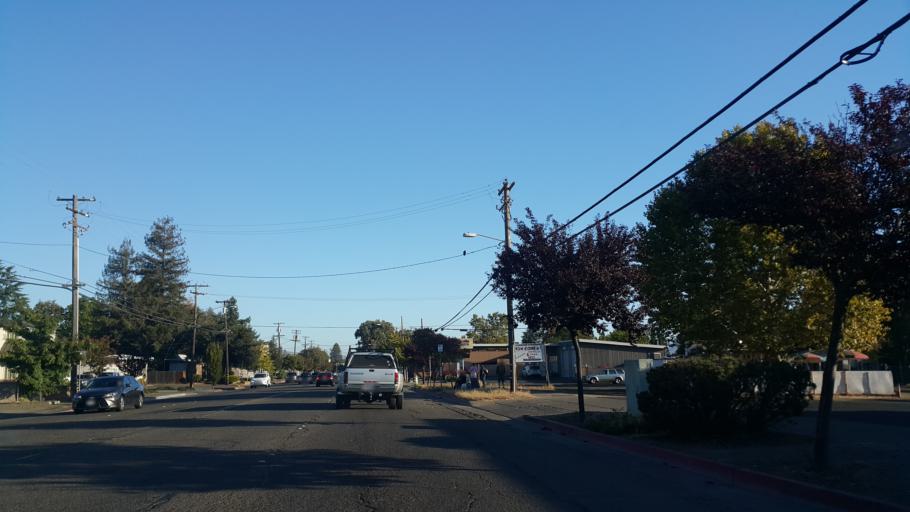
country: US
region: California
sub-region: Mendocino County
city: Ukiah
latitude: 39.1388
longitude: -123.2058
